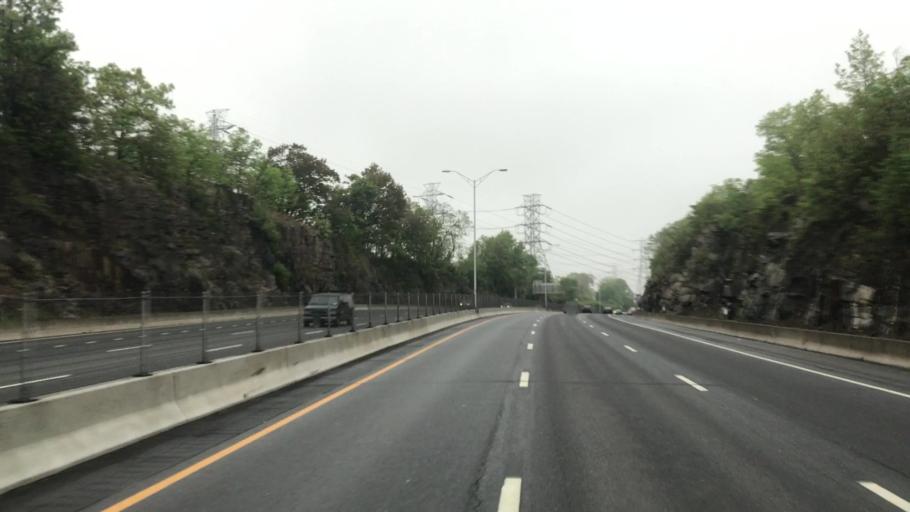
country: US
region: New York
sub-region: Westchester County
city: Bronxville
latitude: 40.9402
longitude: -73.8556
